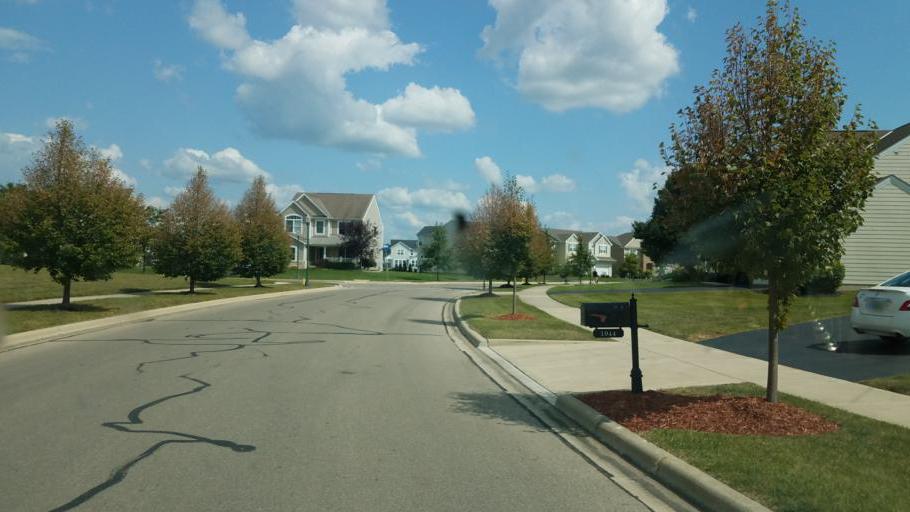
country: US
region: Ohio
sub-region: Delaware County
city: Lewis Center
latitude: 40.2492
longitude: -83.0254
